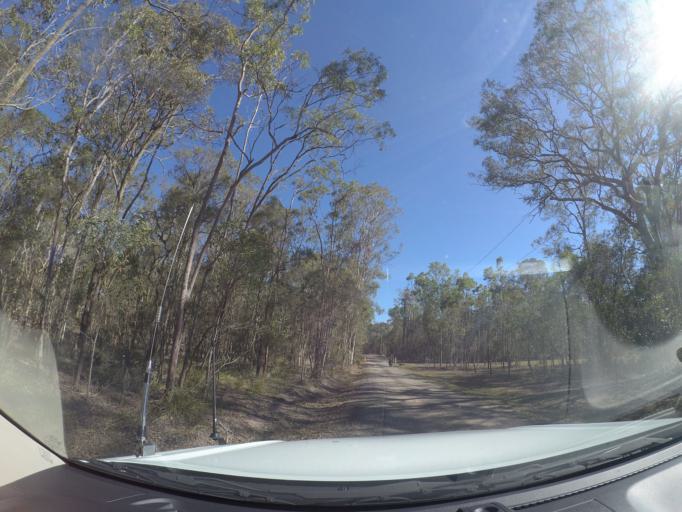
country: AU
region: Queensland
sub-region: Logan
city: Park Ridge South
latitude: -27.7460
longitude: 153.0508
